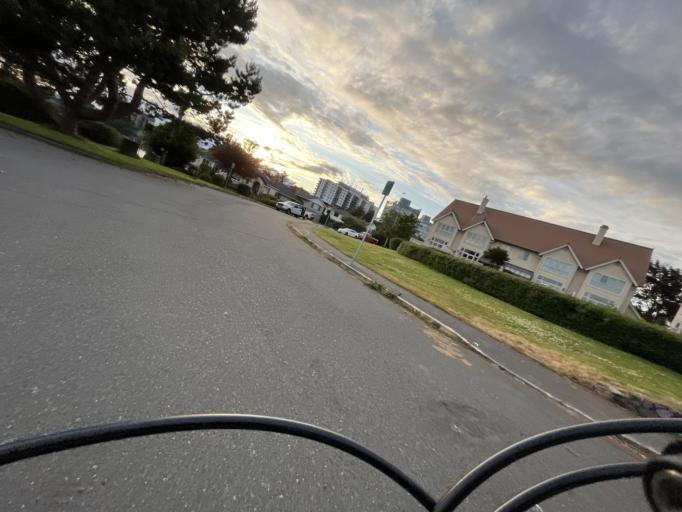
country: CA
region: British Columbia
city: Victoria
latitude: 48.4282
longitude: -123.3884
